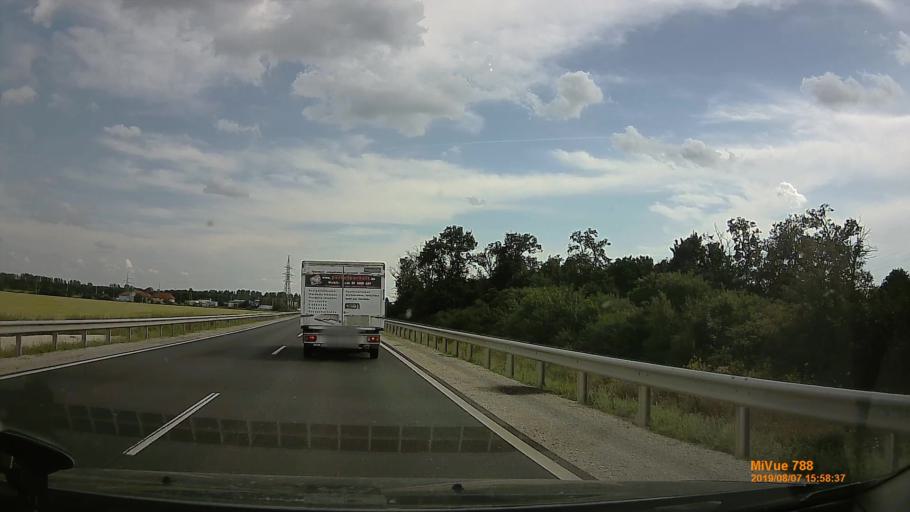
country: HU
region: Vas
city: Kormend
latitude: 47.0246
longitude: 16.6139
